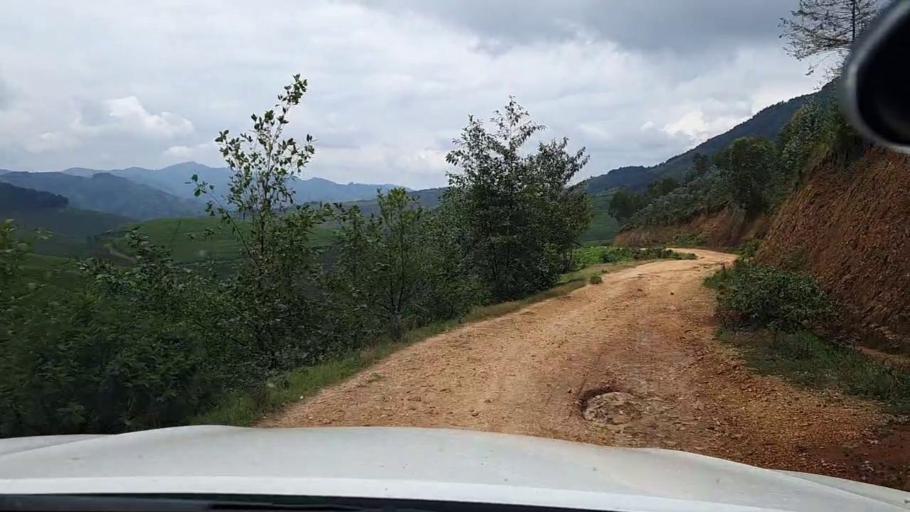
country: RW
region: Western Province
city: Kibuye
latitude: -2.1585
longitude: 29.4539
